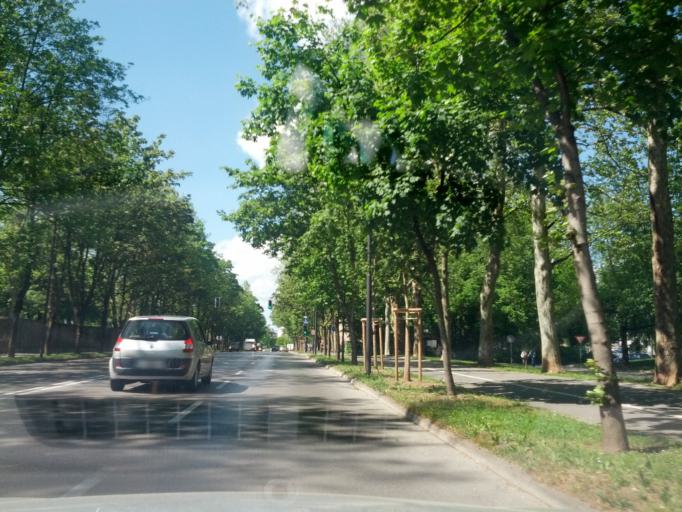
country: SI
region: Ljubljana
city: Ljubljana
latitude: 46.0620
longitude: 14.5200
